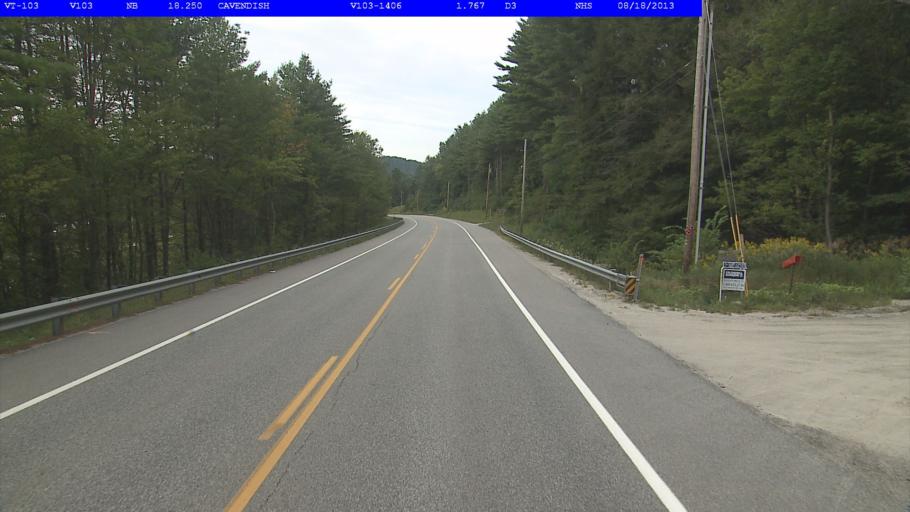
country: US
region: Vermont
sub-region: Windsor County
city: Chester
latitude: 43.3718
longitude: -72.6349
